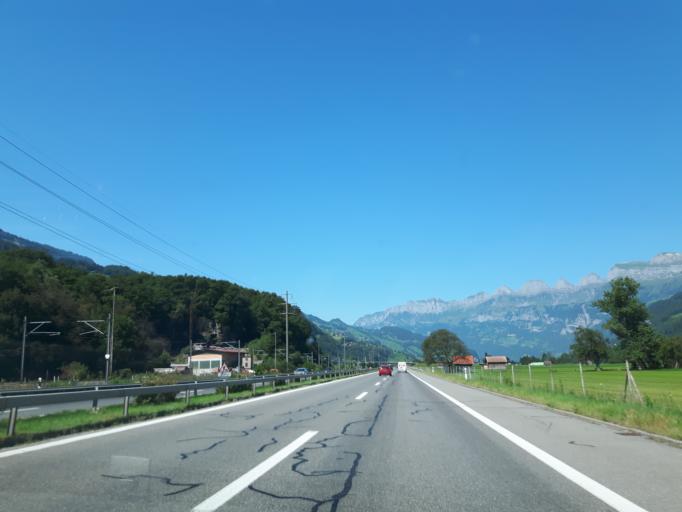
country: CH
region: Saint Gallen
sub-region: Wahlkreis Sarganserland
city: Sargans
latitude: 47.0636
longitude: 9.3971
